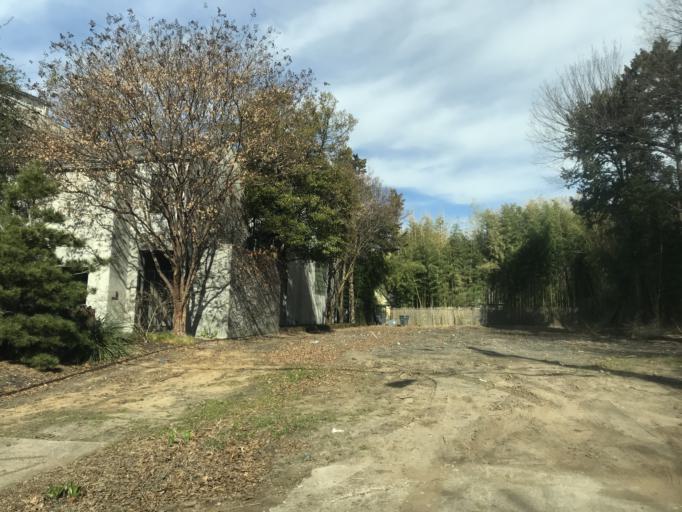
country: US
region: Texas
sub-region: Dallas County
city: Highland Park
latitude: 32.8197
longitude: -96.7947
